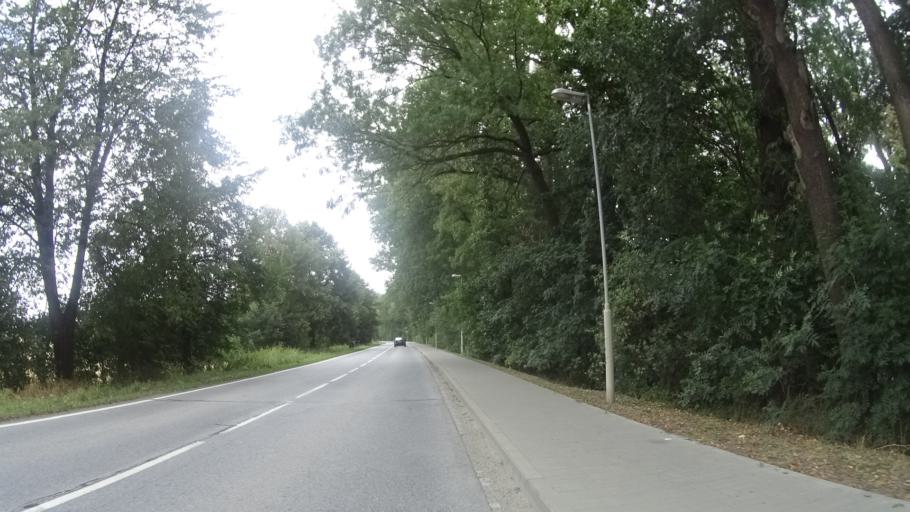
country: CZ
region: Olomoucky
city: Tovacov
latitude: 49.4215
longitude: 17.2904
